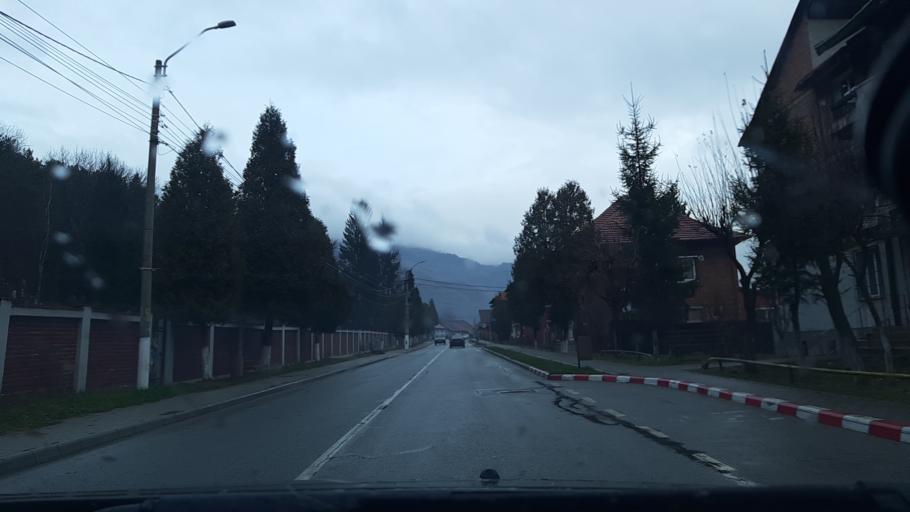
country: RO
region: Hunedoara
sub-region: Municipiul Petrosani
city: Petrosani
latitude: 45.4389
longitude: 23.3686
